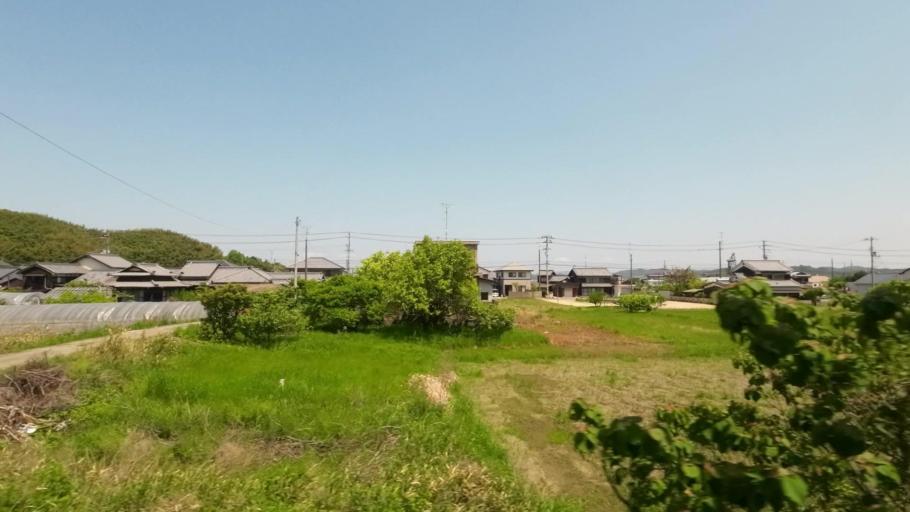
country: JP
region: Ehime
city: Hojo
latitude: 34.0623
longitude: 132.9016
